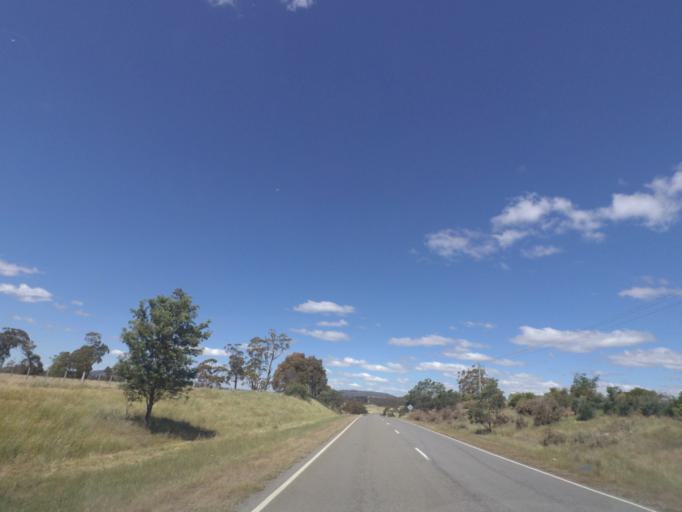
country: AU
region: Victoria
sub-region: Mount Alexander
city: Castlemaine
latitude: -37.2914
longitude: 144.4903
